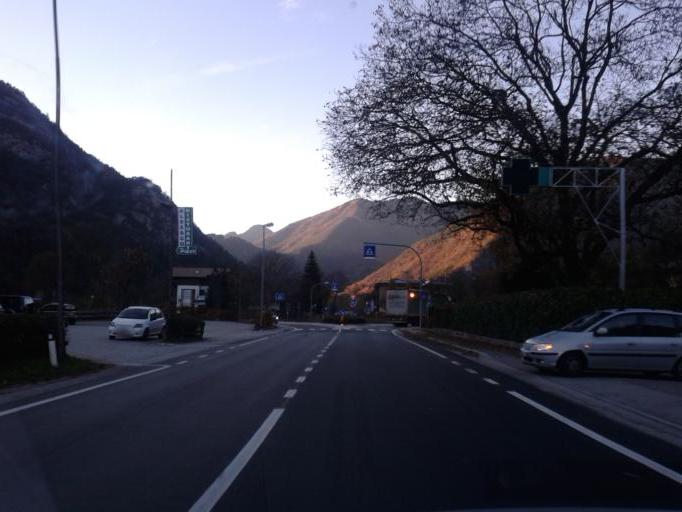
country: IT
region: Trentino-Alto Adige
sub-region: Provincia di Trento
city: Pieve di Ledro
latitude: 45.8883
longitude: 10.7321
